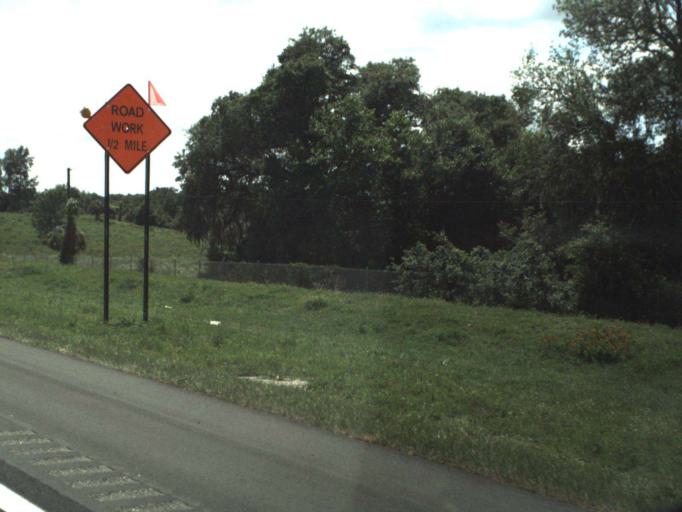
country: US
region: Florida
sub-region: Seminole County
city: Heathrow
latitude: 28.7251
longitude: -81.3745
